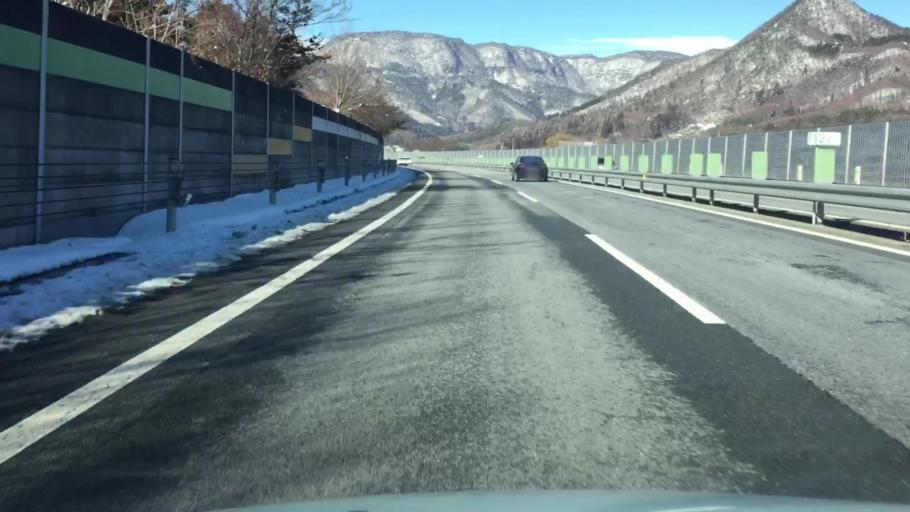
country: JP
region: Gunma
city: Numata
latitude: 36.6669
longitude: 139.0643
